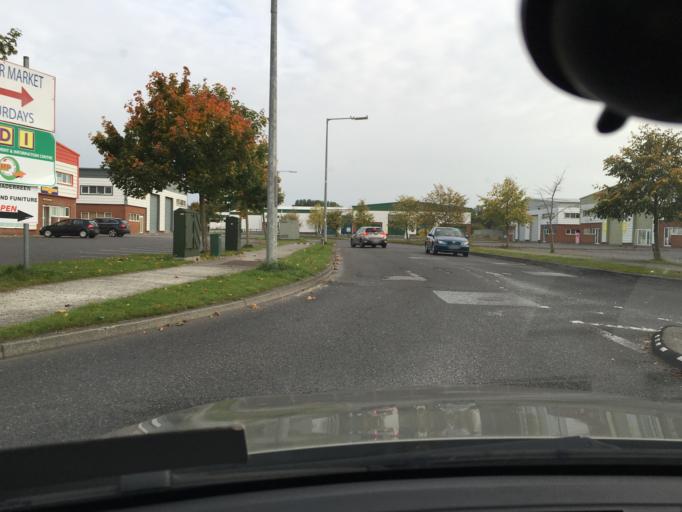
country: IE
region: Leinster
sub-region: An Longfort
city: Longford
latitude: 53.7218
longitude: -7.8084
